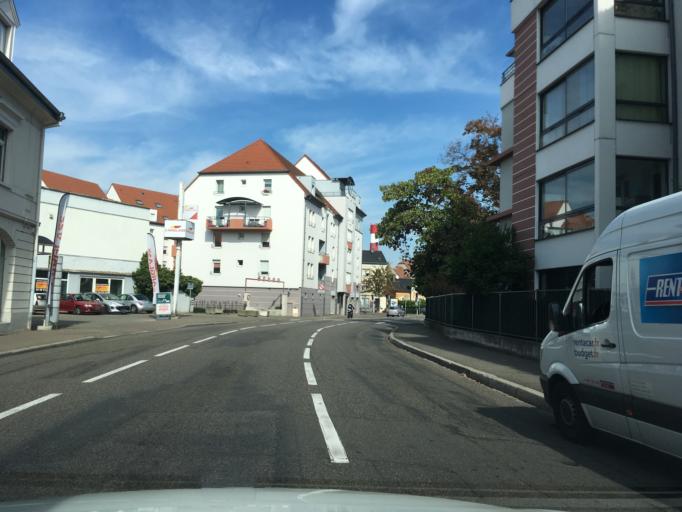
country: FR
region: Alsace
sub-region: Departement du Haut-Rhin
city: Colmar
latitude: 48.0807
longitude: 7.3528
